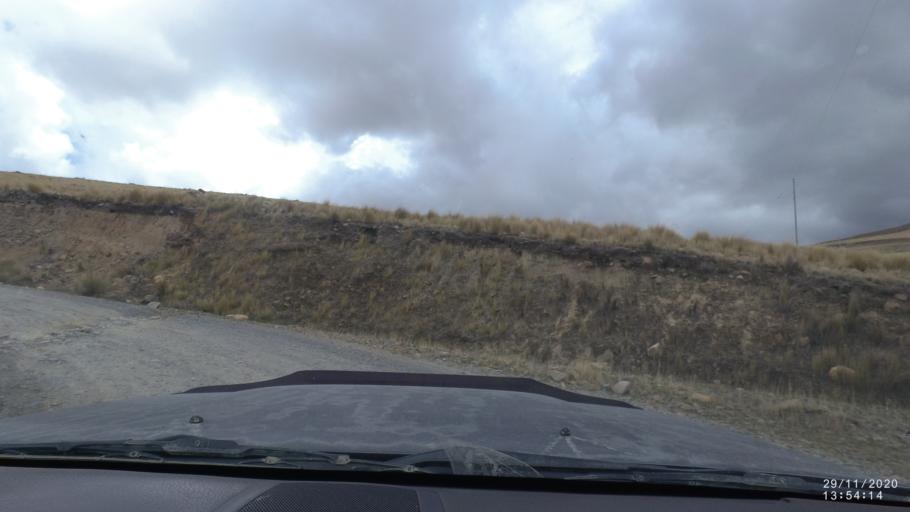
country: BO
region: Cochabamba
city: Sipe Sipe
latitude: -17.1728
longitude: -66.3561
